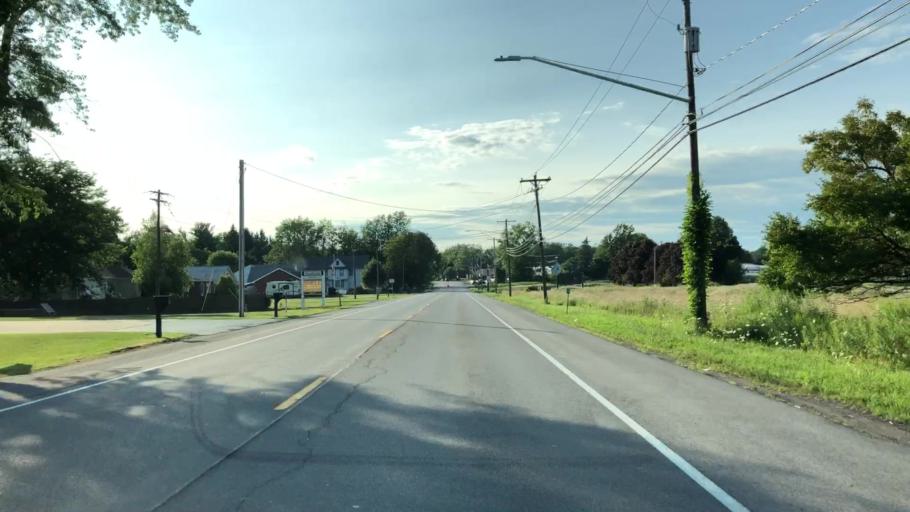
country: US
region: New York
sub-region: Erie County
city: West Seneca
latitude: 42.8655
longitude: -78.7723
